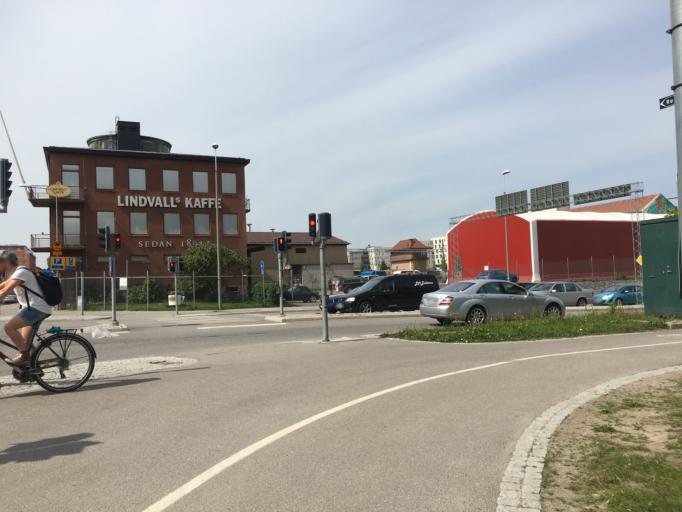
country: SE
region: Uppsala
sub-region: Uppsala Kommun
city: Uppsala
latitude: 59.8545
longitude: 17.6514
